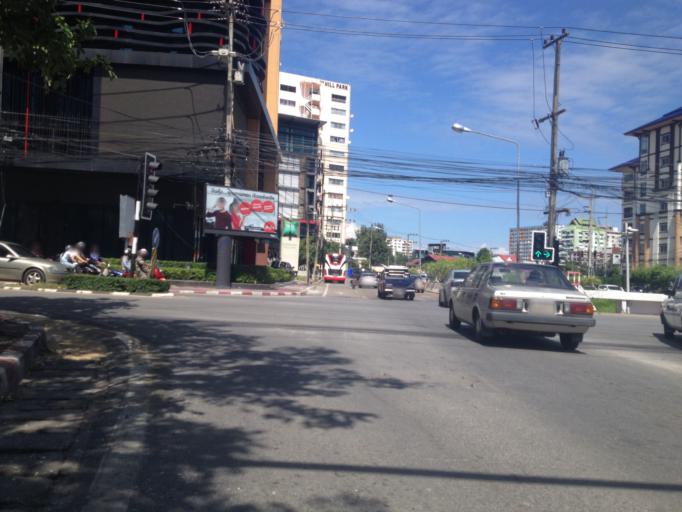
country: TH
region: Chiang Mai
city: Chiang Mai
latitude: 18.8054
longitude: 98.9600
